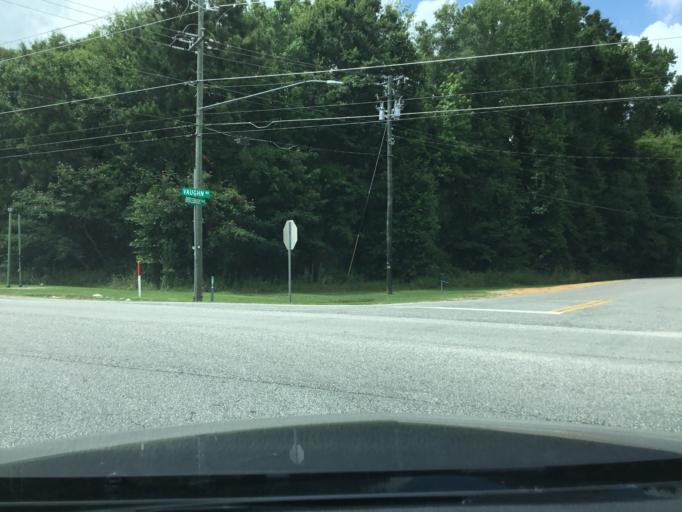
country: US
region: Alabama
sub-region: Montgomery County
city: Pike Road
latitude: 32.3469
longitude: -86.0852
